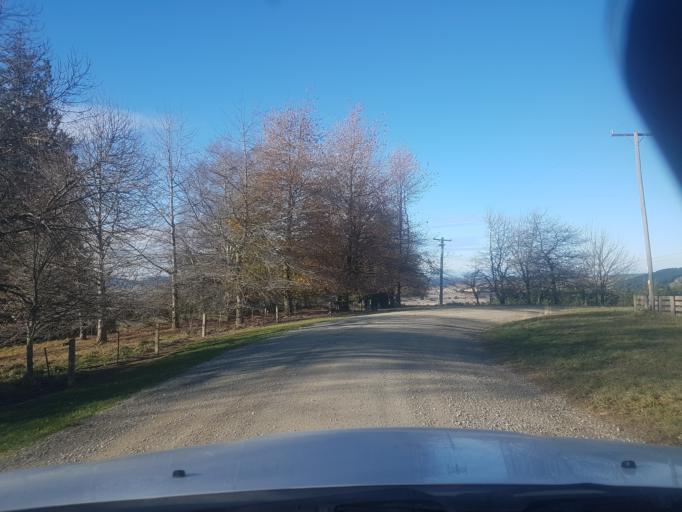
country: NZ
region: Canterbury
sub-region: Timaru District
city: Pleasant Point
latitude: -44.1693
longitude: 170.9253
